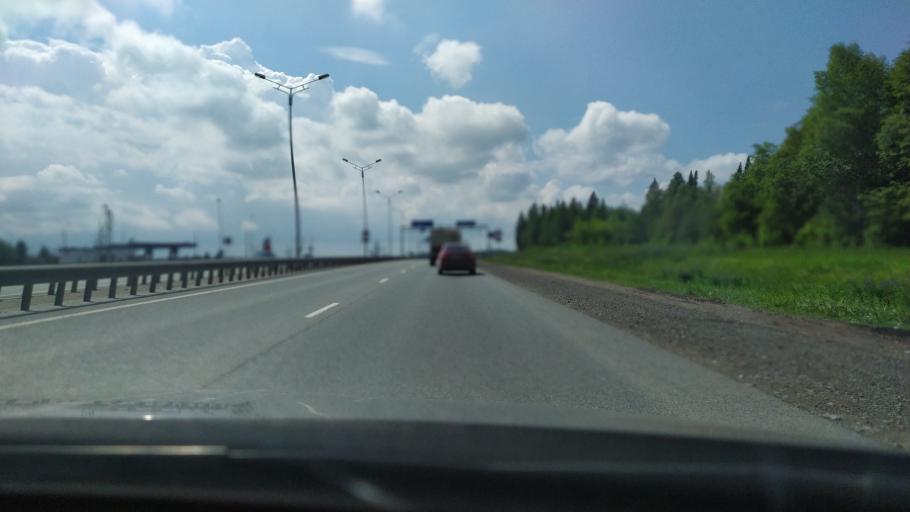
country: RU
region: Perm
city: Ferma
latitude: 58.0031
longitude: 56.3911
